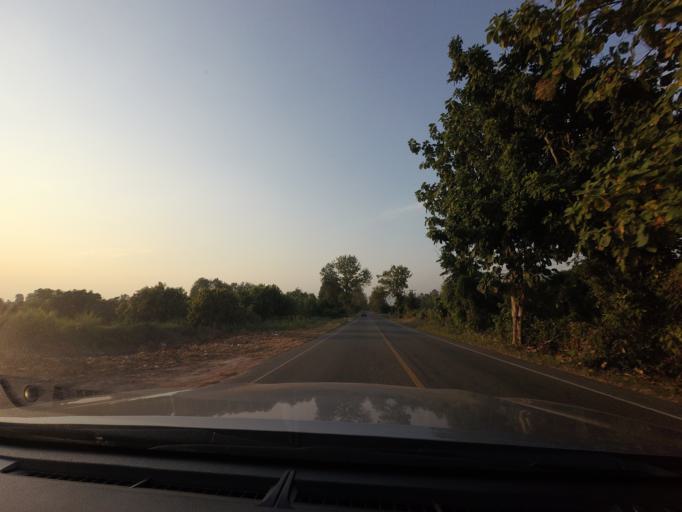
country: TH
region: Phitsanulok
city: Wang Thong
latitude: 16.6917
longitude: 100.5238
